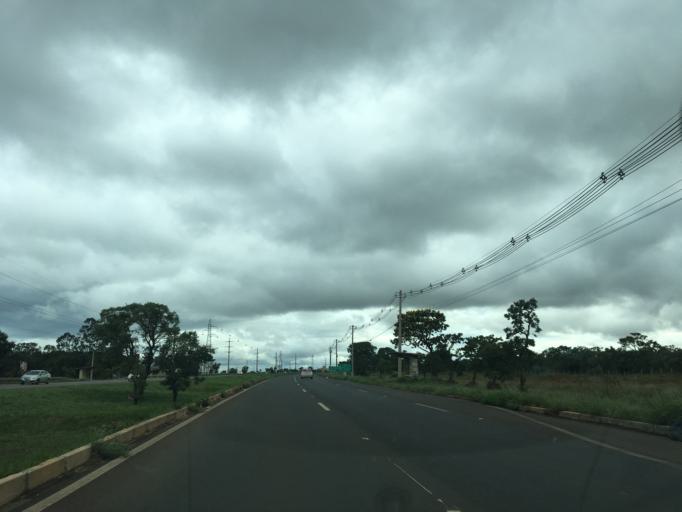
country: BR
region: Federal District
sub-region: Brasilia
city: Brasilia
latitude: -15.8966
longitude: -47.8197
